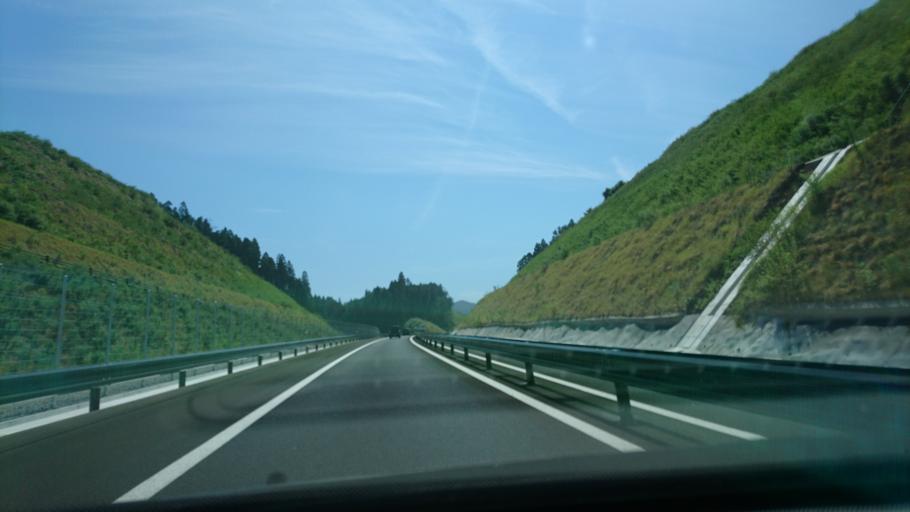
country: JP
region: Iwate
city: Ofunato
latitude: 39.0005
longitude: 141.6147
